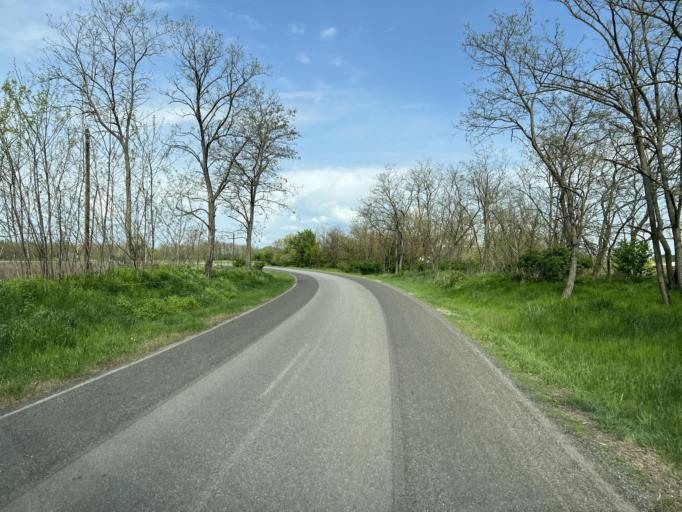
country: HU
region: Pest
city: Cegledbercel
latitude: 47.1626
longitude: 19.6162
